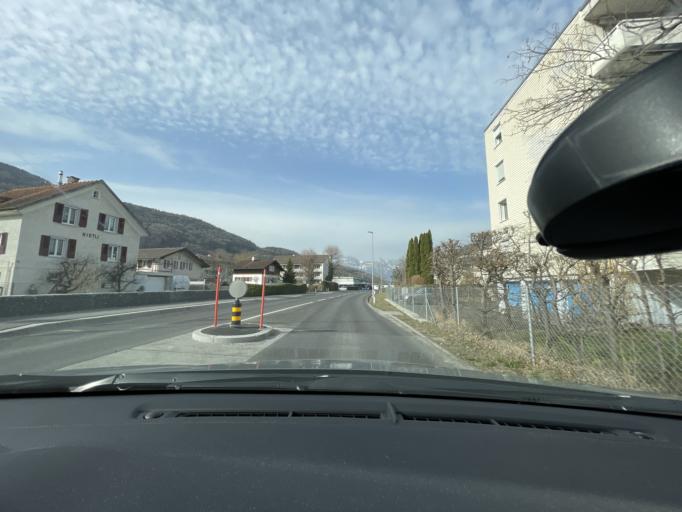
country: CH
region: Saint Gallen
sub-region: Wahlkreis Werdenberg
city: Sevelen
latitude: 47.1261
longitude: 9.4863
